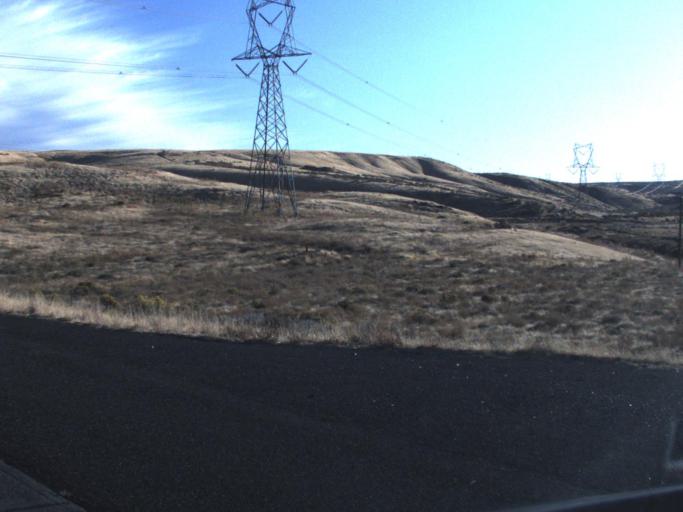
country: US
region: Washington
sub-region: Franklin County
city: Basin City
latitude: 46.5435
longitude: -119.0084
